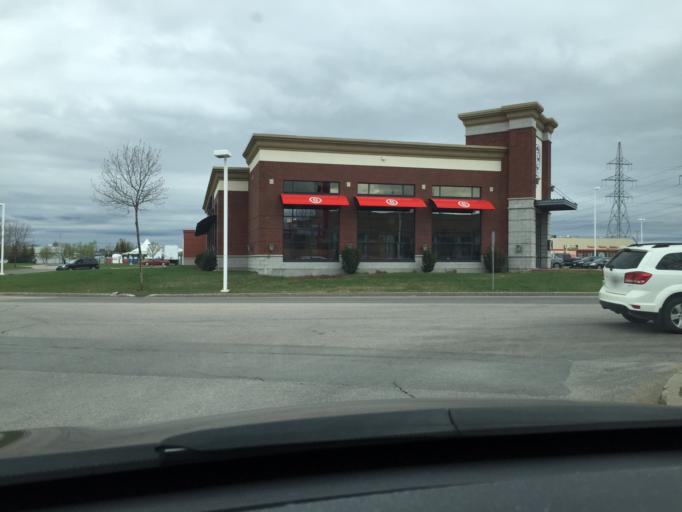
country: CA
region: Quebec
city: Quebec
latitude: 46.8417
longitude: -71.2732
